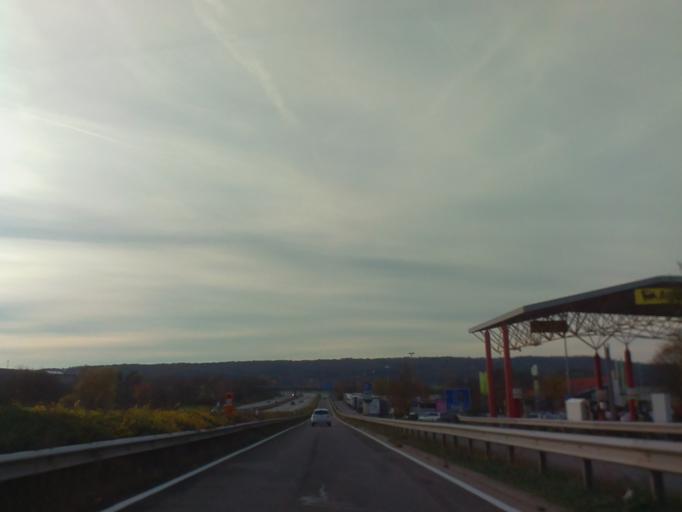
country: DE
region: Rheinland-Pfalz
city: Hettenleidelheim
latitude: 49.5271
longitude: 8.0747
